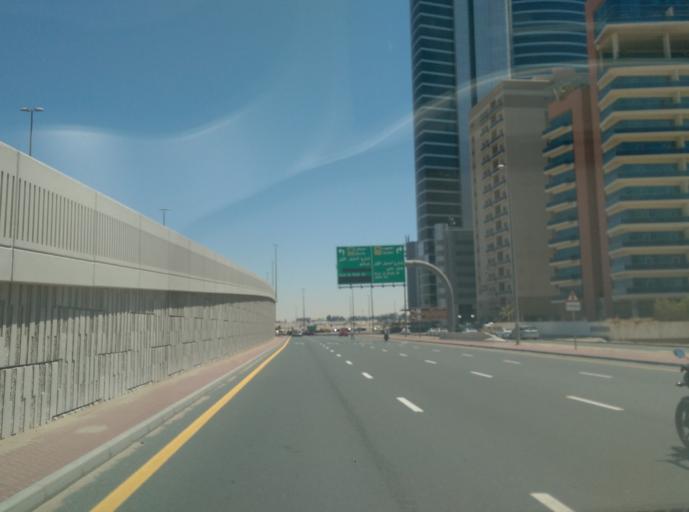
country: AE
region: Dubai
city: Dubai
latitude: 25.0993
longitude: 55.1806
